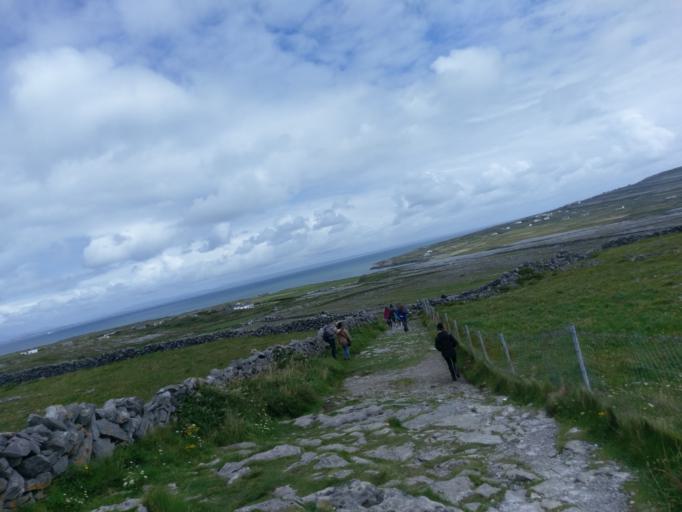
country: IE
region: Connaught
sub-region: County Galway
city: Clifden
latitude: 53.1261
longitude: -9.7647
